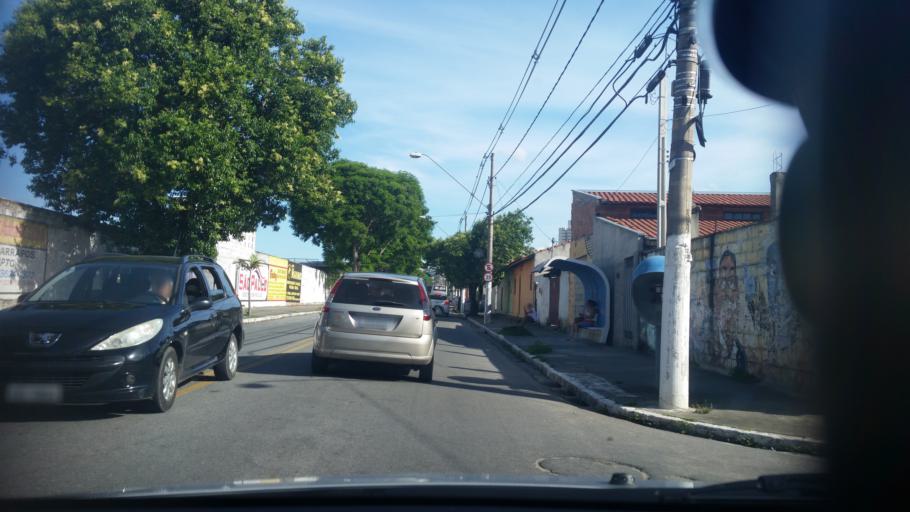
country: BR
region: Sao Paulo
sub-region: Taubate
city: Taubate
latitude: -23.0167
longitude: -45.5740
